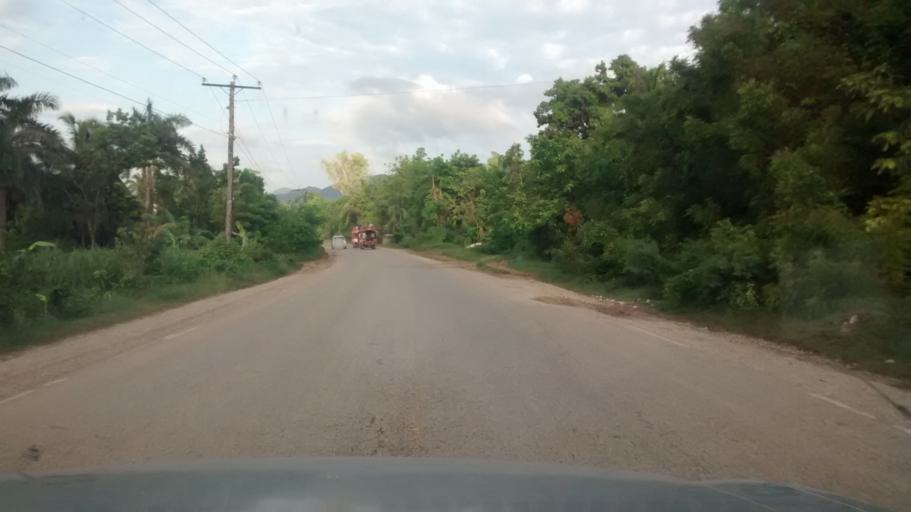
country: HT
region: Ouest
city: Tigwav
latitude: 18.4201
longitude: -72.9587
